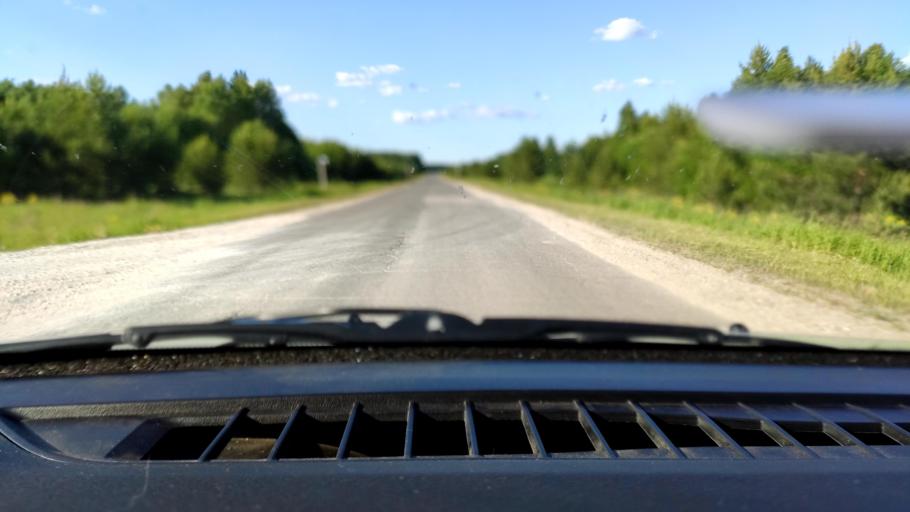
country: RU
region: Perm
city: Uinskoye
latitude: 57.1134
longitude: 56.6671
